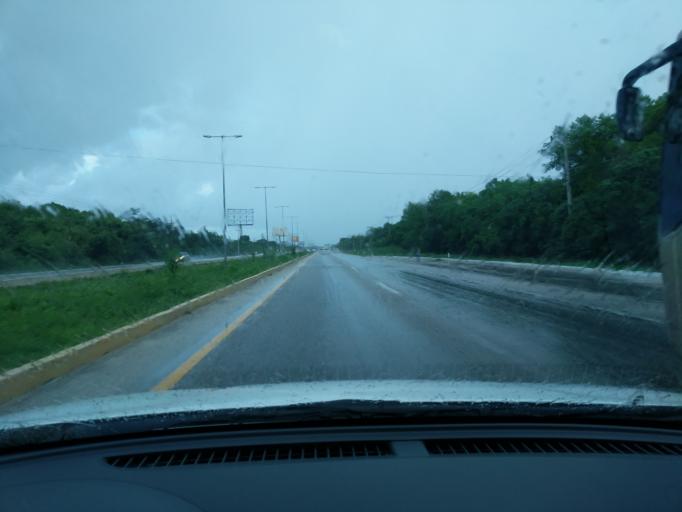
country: MX
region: Quintana Roo
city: Alfredo V. Bonfil
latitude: 20.8995
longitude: -86.8804
